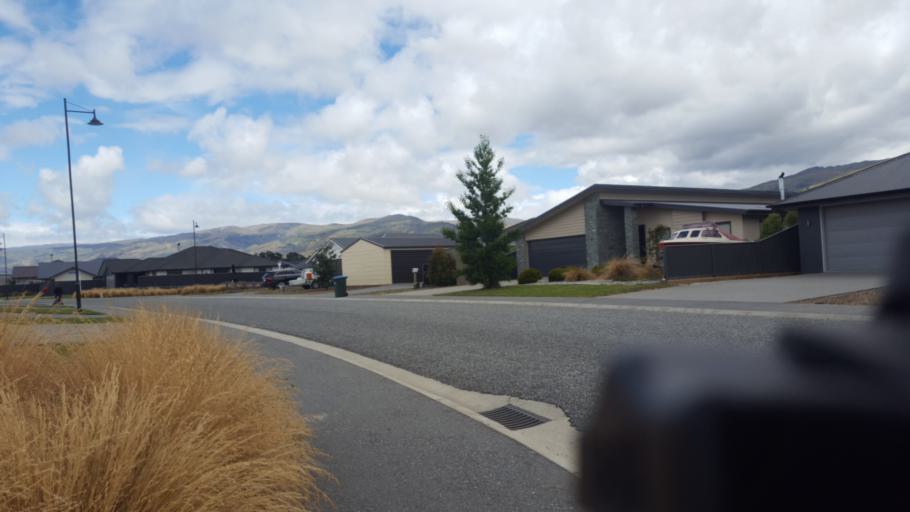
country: NZ
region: Otago
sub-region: Queenstown-Lakes District
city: Wanaka
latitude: -45.0466
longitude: 169.1800
